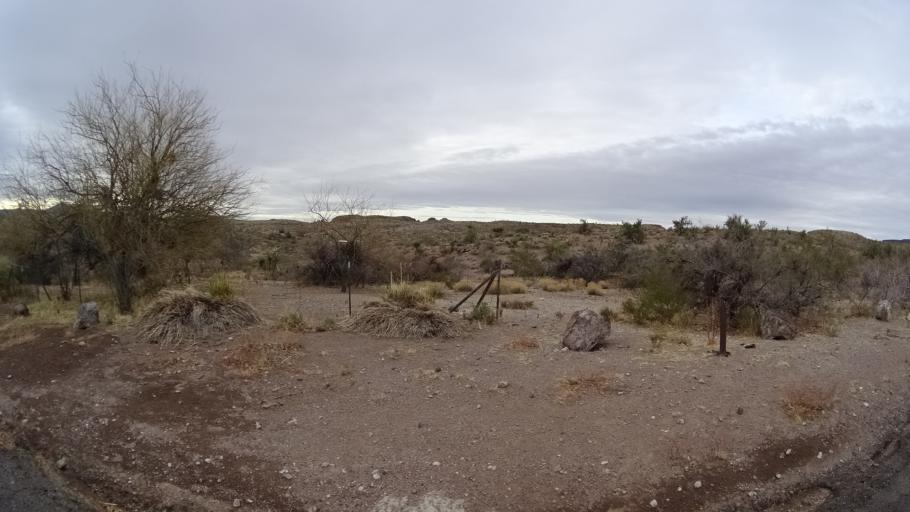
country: US
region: Arizona
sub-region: Mohave County
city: Kingman
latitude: 35.2029
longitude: -114.0763
